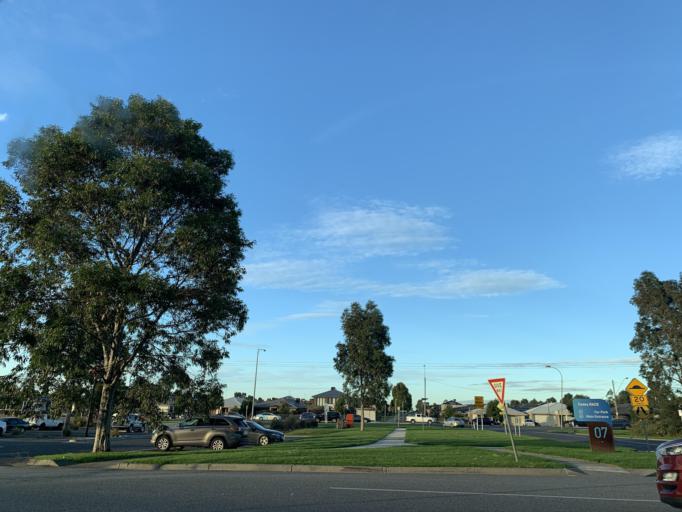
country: AU
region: Victoria
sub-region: Casey
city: Cranbourne East
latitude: -38.1140
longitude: 145.2968
